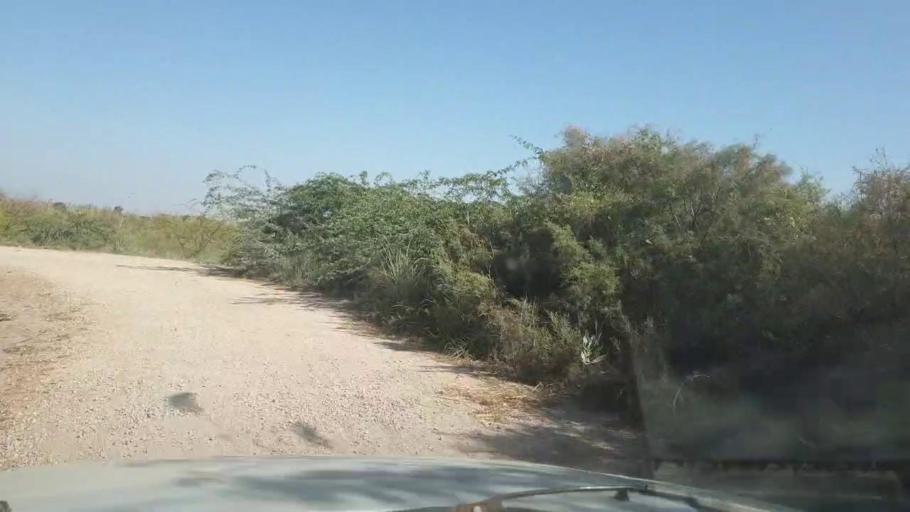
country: PK
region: Sindh
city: Mirpur Sakro
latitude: 24.4640
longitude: 67.7645
